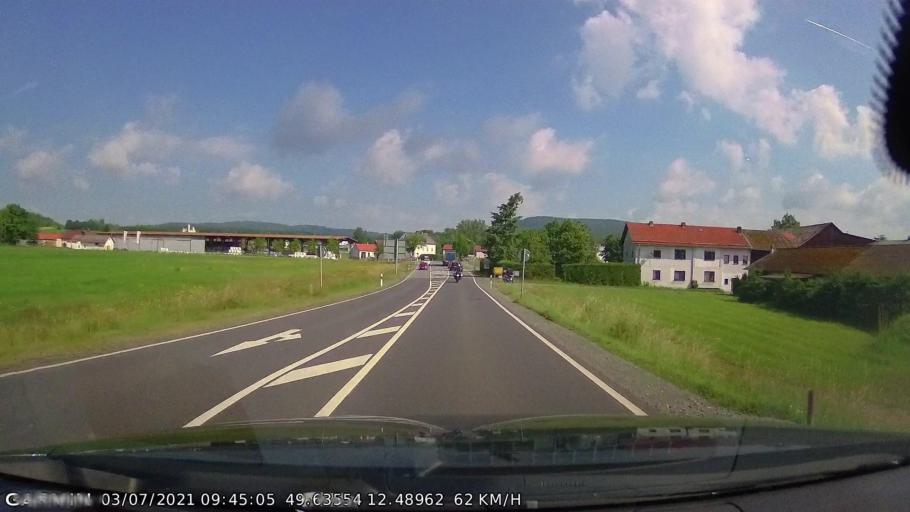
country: DE
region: Bavaria
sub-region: Upper Palatinate
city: Waidhaus
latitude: 49.6356
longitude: 12.4896
